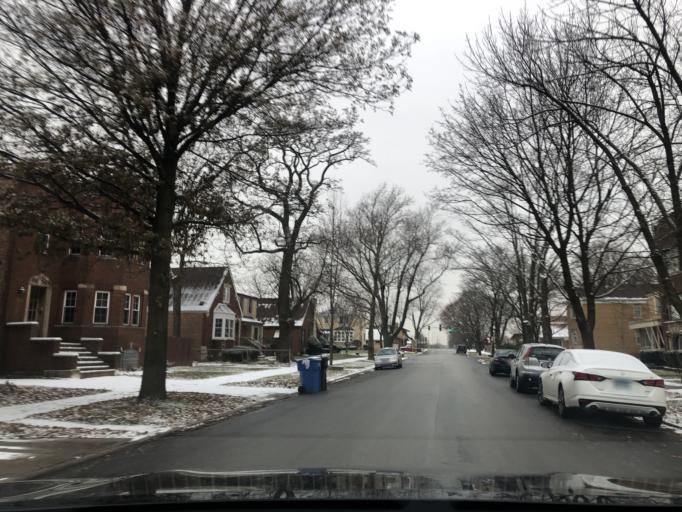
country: US
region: Illinois
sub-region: Cook County
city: Evergreen Park
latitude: 41.7283
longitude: -87.6800
